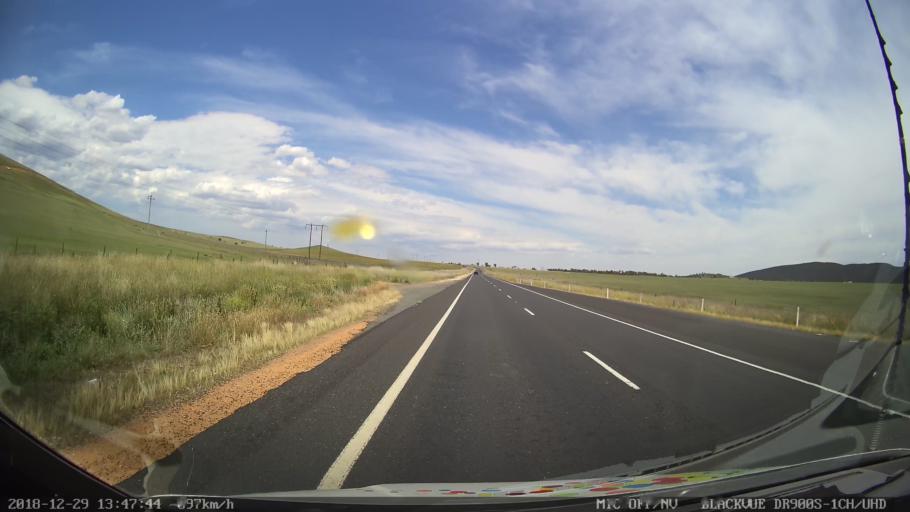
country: AU
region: New South Wales
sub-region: Cooma-Monaro
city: Cooma
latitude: -36.1307
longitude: 149.1443
